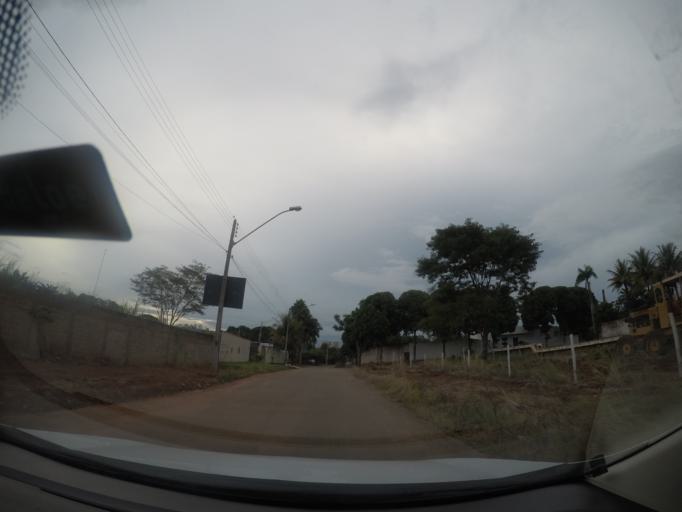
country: BR
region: Goias
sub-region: Goiania
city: Goiania
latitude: -16.6548
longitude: -49.2272
